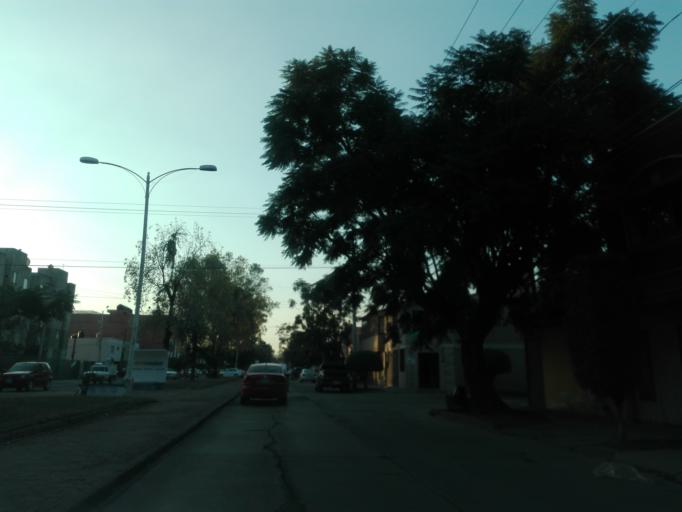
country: MX
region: Guanajuato
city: Leon
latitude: 21.1053
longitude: -101.6651
